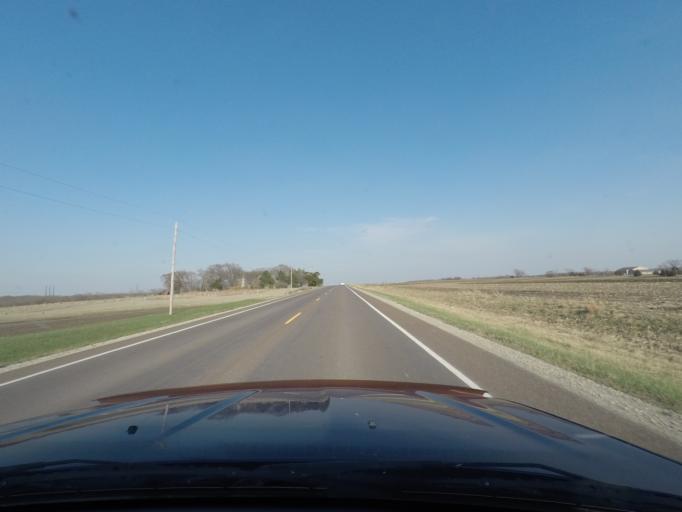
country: US
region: Kansas
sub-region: Douglas County
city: Lawrence
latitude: 39.0006
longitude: -95.3221
